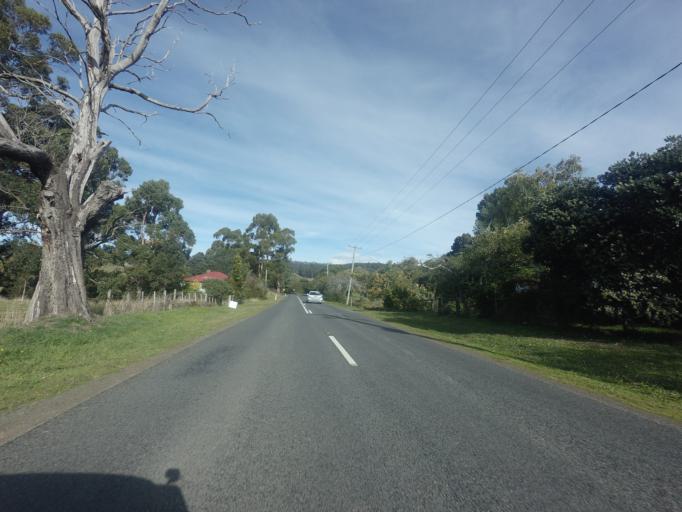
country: AU
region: Tasmania
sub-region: Clarence
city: Sandford
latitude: -43.0606
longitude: 147.8112
